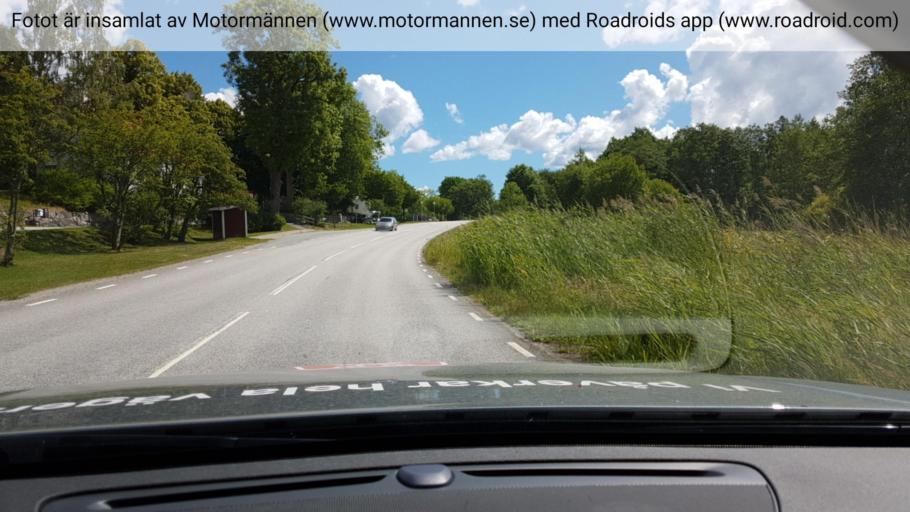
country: SE
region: Stockholm
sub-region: Varmdo Kommun
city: Hemmesta
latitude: 59.3578
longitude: 18.4945
